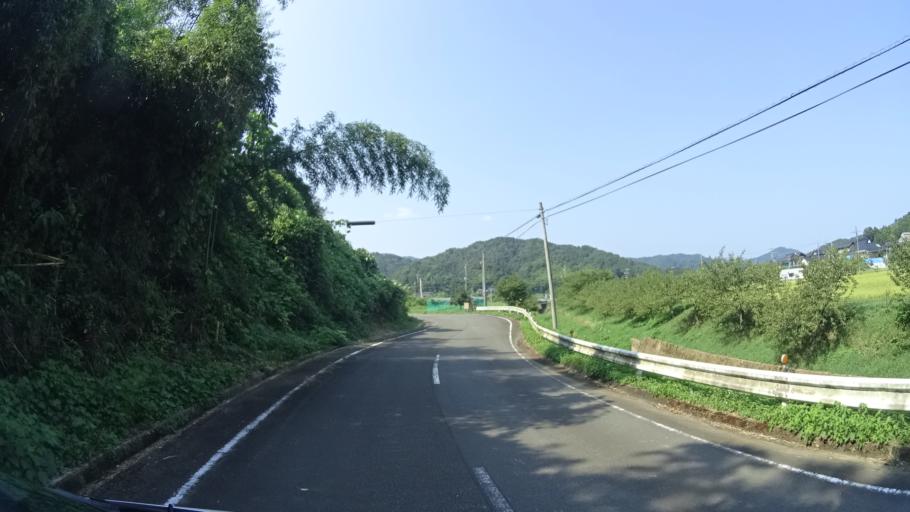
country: JP
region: Kyoto
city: Ayabe
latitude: 35.4074
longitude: 135.1969
